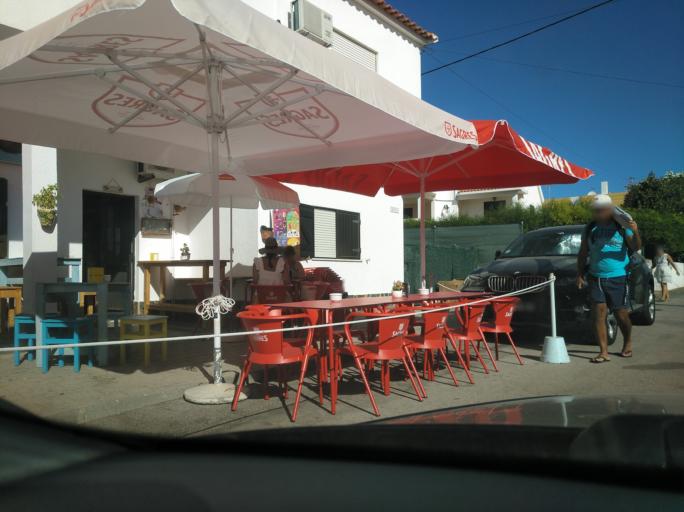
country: PT
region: Faro
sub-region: Vila Real de Santo Antonio
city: Monte Gordo
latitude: 37.1691
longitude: -7.5128
